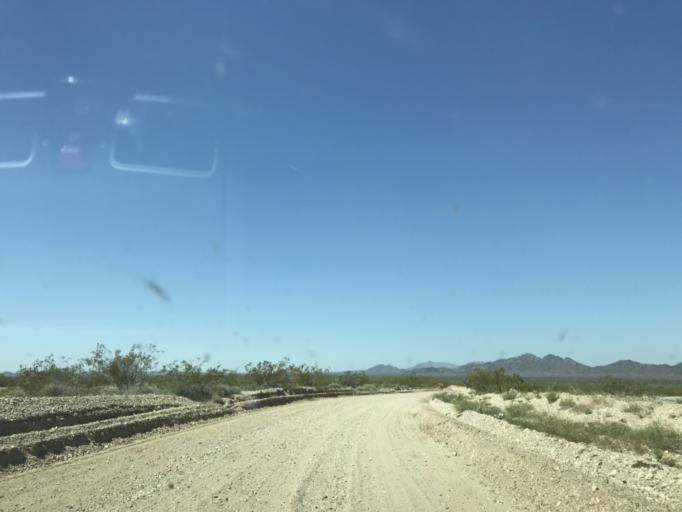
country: US
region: California
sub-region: Riverside County
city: Mesa Verde
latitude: 33.4956
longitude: -114.8752
